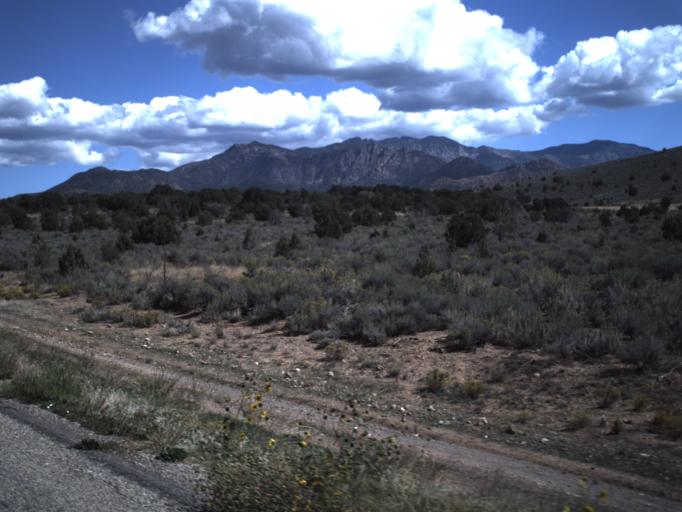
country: US
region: Utah
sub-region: Washington County
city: Ivins
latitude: 37.3565
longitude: -113.6798
